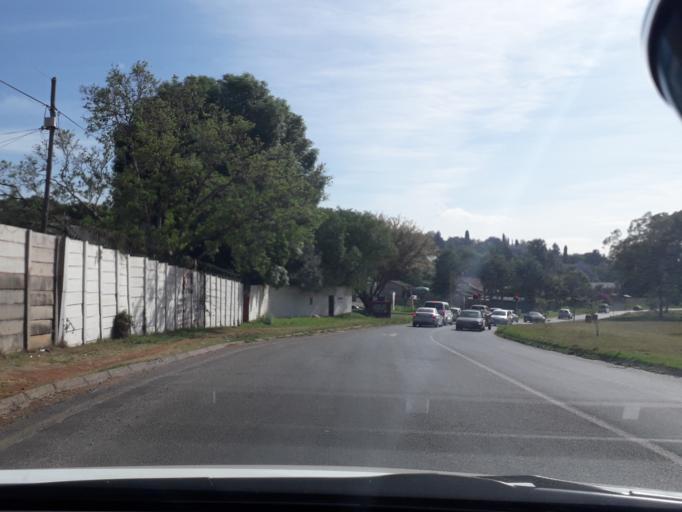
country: ZA
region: Gauteng
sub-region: City of Johannesburg Metropolitan Municipality
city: Roodepoort
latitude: -26.1201
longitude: 27.9244
